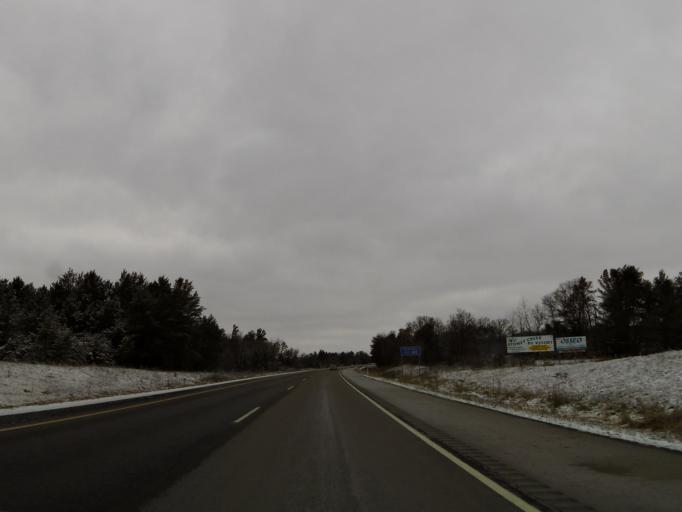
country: US
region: Wisconsin
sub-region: Trempealeau County
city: Osseo
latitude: 44.5682
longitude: -91.1929
